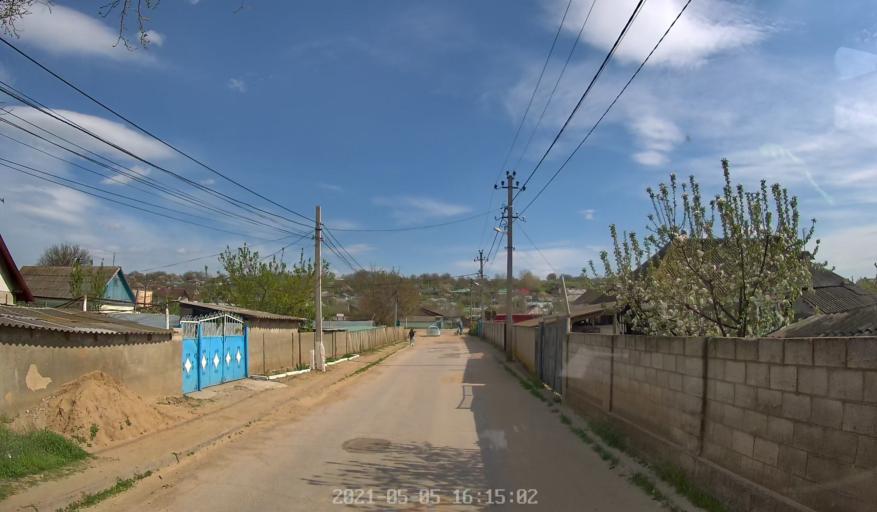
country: MD
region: Criuleni
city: Criuleni
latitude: 47.1348
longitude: 29.2026
